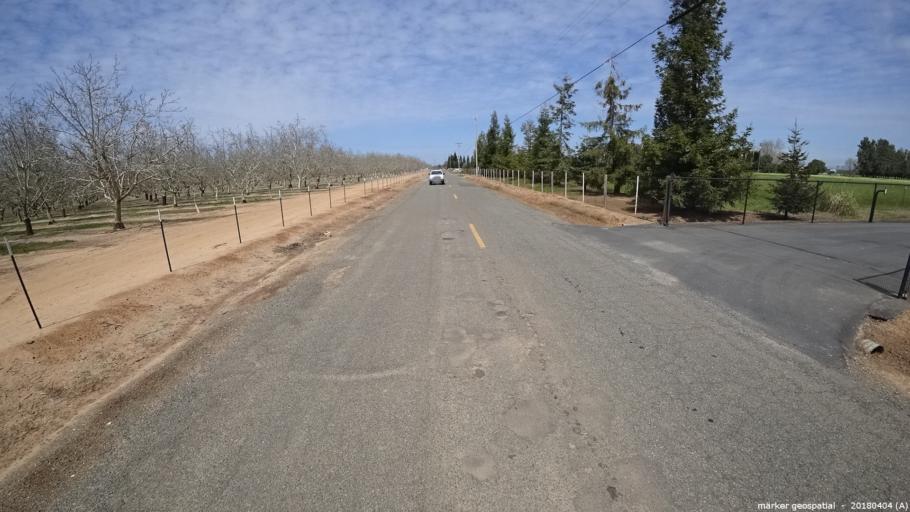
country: US
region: California
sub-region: Sacramento County
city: Herald
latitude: 38.2986
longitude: -121.2080
